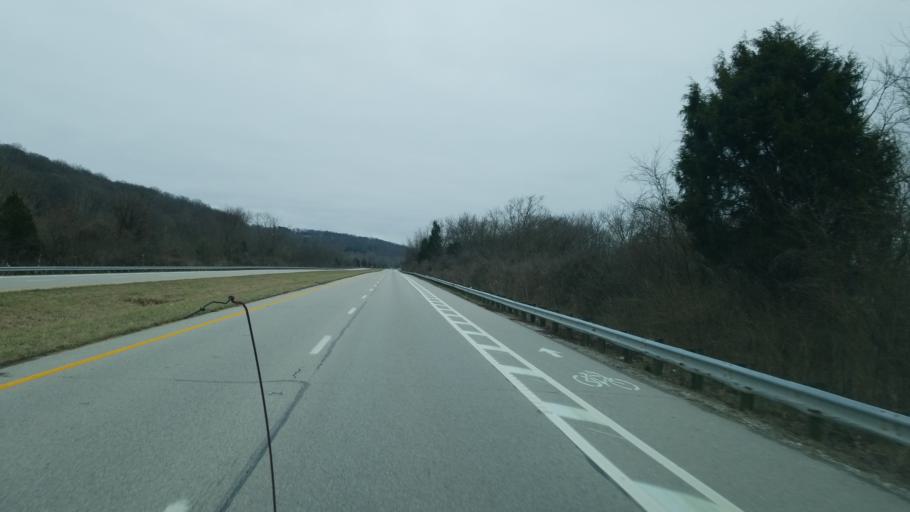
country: US
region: Ohio
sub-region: Hamilton County
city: Cherry Grove
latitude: 39.0307
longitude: -84.3285
